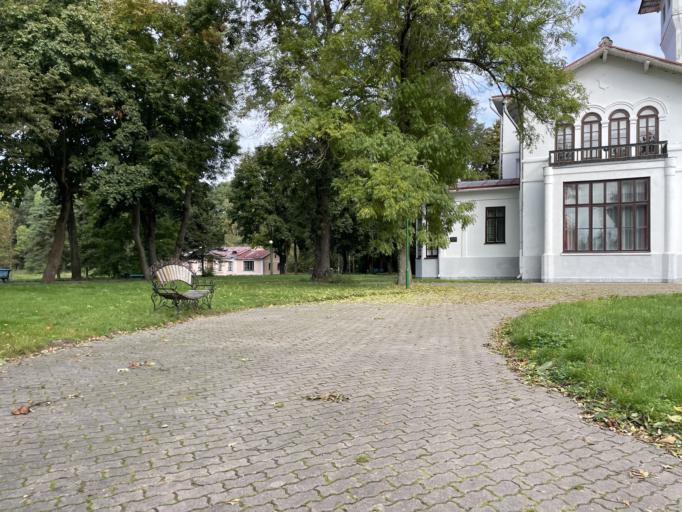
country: BY
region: Brest
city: Pruzhany
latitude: 52.5649
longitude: 24.4573
